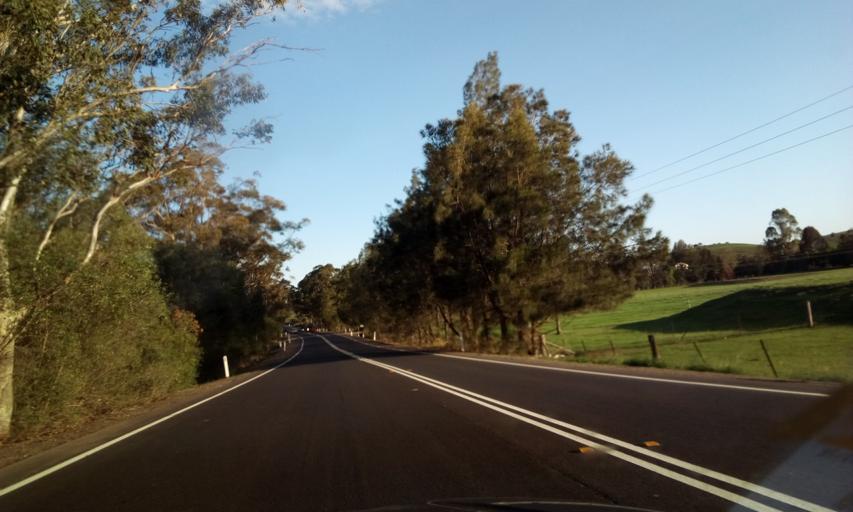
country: AU
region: New South Wales
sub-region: Camden
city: Camden South
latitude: -34.1253
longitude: 150.7011
